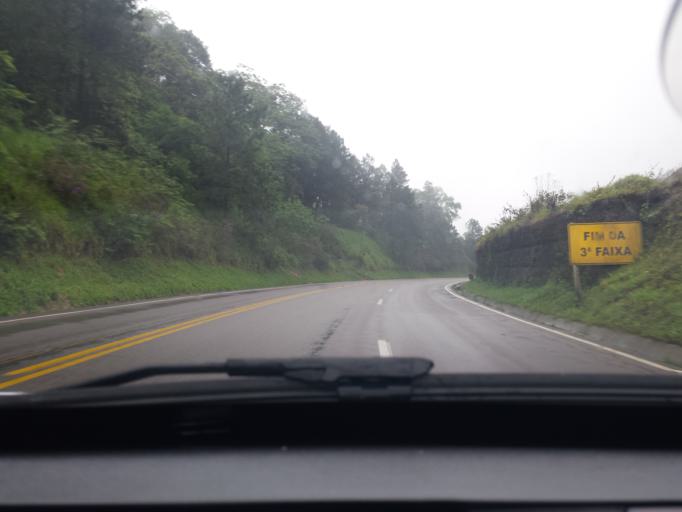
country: BR
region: Santa Catarina
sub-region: Itajai
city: Itajai
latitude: -26.8391
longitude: -48.7664
